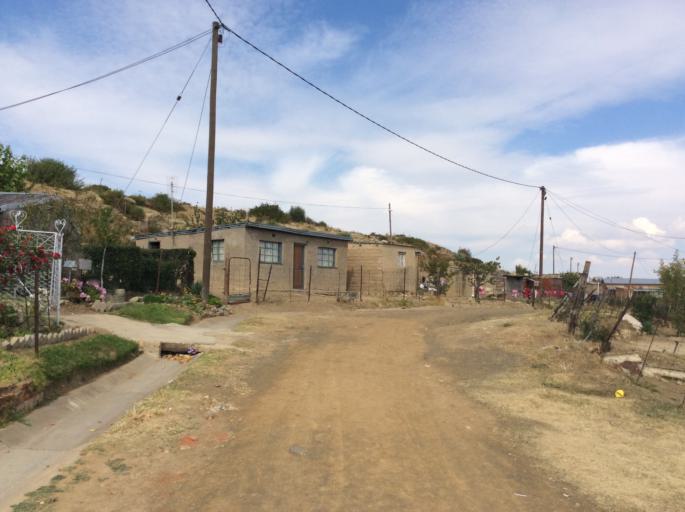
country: ZA
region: Orange Free State
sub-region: Xhariep District Municipality
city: Dewetsdorp
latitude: -29.5867
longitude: 26.6816
